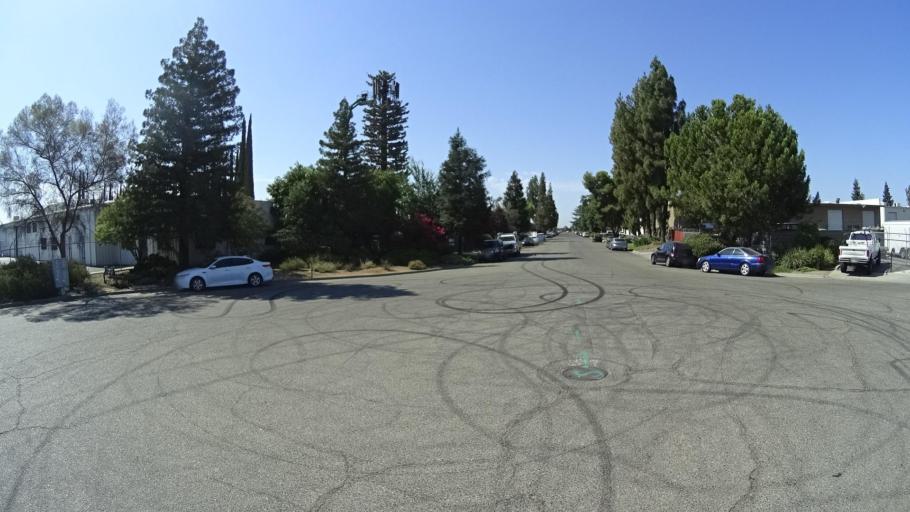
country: US
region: California
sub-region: Fresno County
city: Tarpey Village
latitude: 36.7769
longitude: -119.6976
